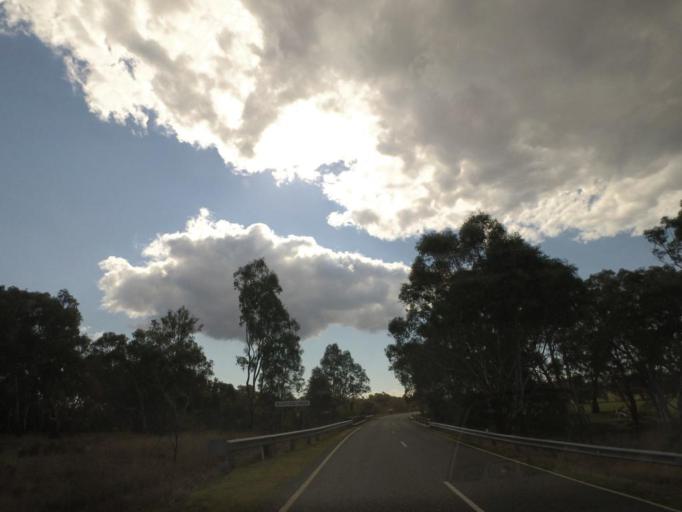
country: AU
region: New South Wales
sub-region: Corowa Shire
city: Howlong
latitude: -36.1811
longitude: 146.6067
